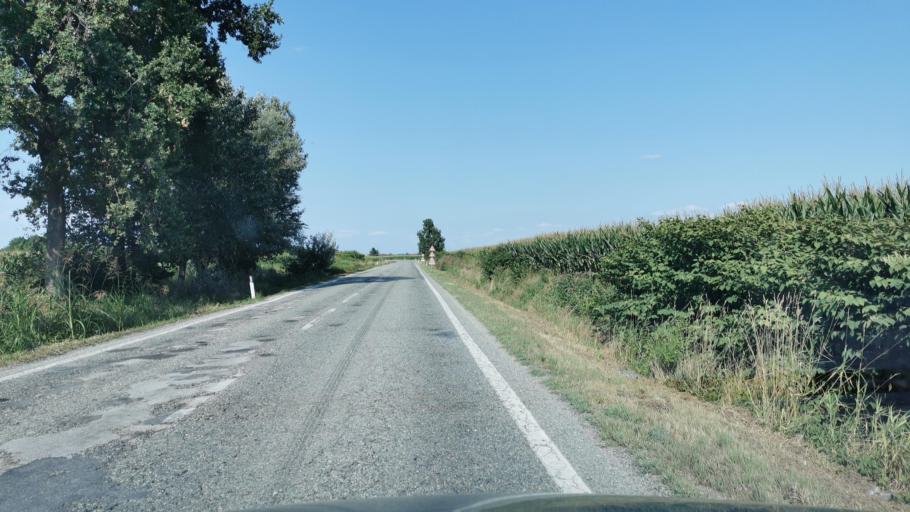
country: IT
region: Piedmont
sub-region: Provincia di Cuneo
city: Revello
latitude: 44.6969
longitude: 7.4289
